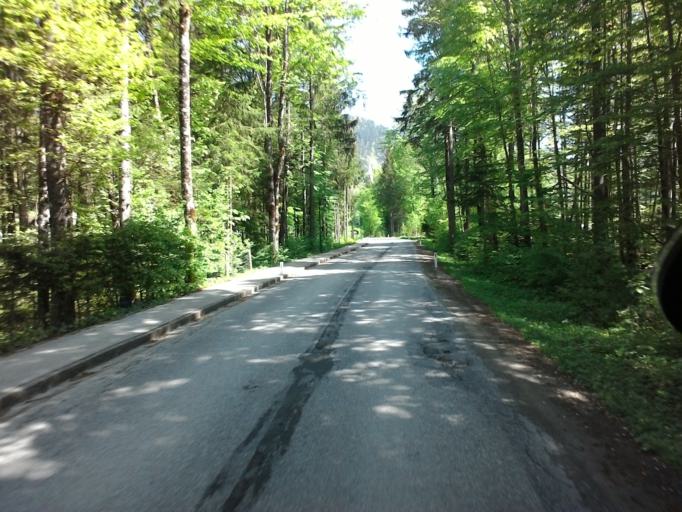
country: AT
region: Styria
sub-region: Politischer Bezirk Liezen
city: Palfau
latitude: 47.7063
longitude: 14.7967
